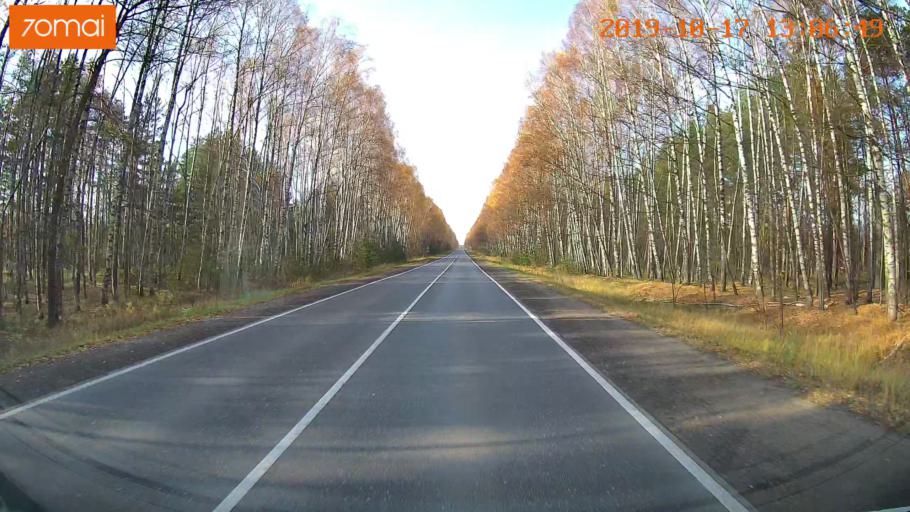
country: RU
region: Rjazan
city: Syntul
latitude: 54.9777
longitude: 41.3054
